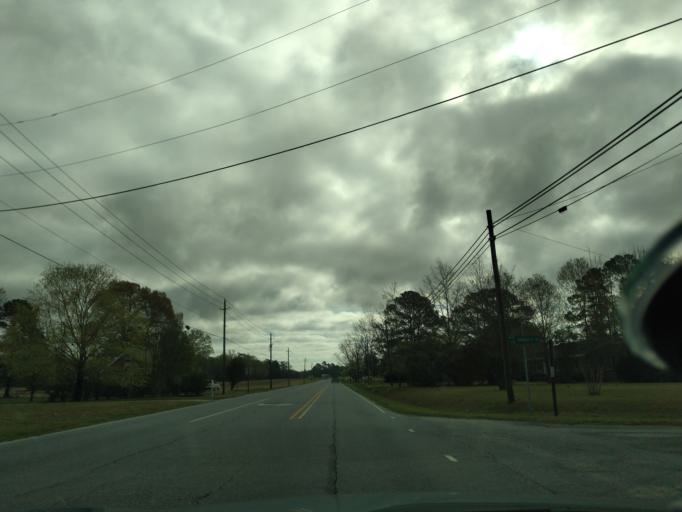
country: US
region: North Carolina
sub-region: Chowan County
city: Edenton
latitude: 36.0570
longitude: -76.6526
